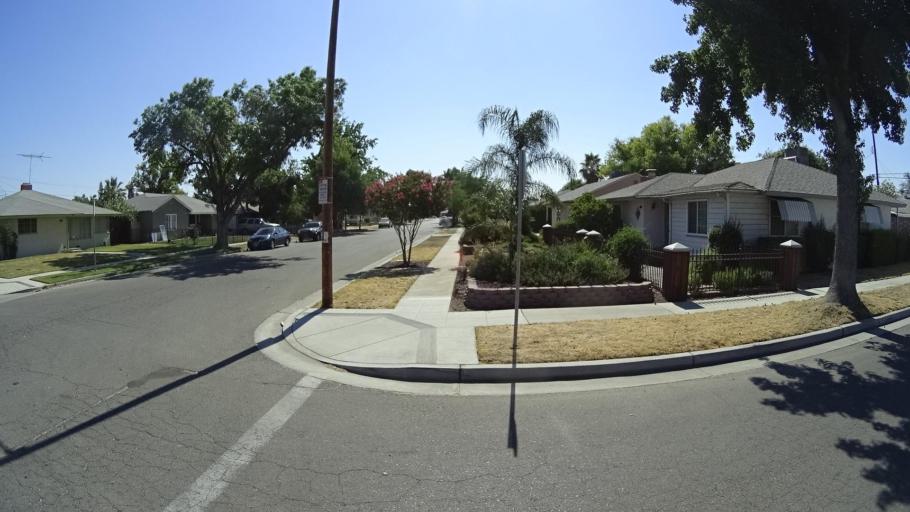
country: US
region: California
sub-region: Fresno County
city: Fresno
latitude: 36.7749
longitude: -119.7747
